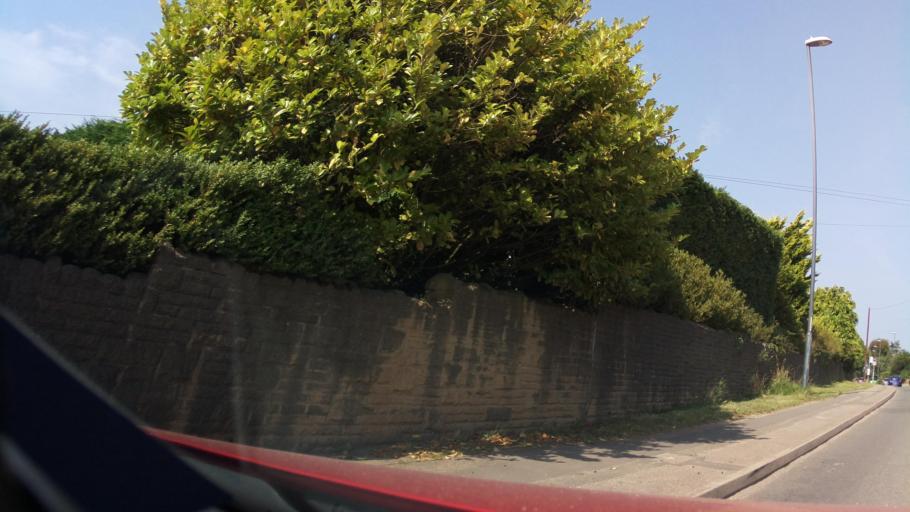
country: GB
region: England
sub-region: Derby
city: Derby
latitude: 52.9468
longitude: -1.5044
